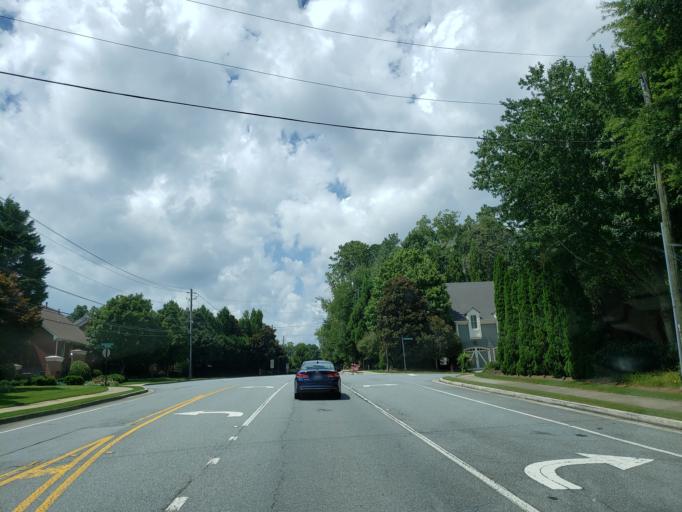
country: US
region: Georgia
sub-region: DeKalb County
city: North Atlanta
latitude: 33.9013
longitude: -84.3475
